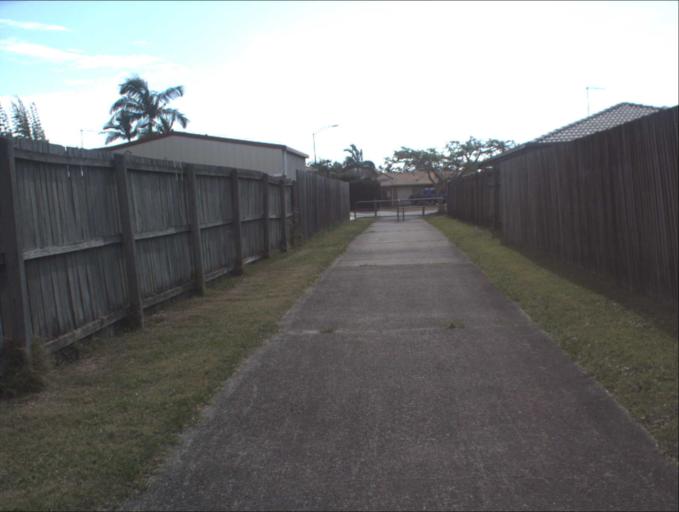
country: AU
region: Queensland
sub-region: Logan
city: Beenleigh
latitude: -27.6836
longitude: 153.1777
